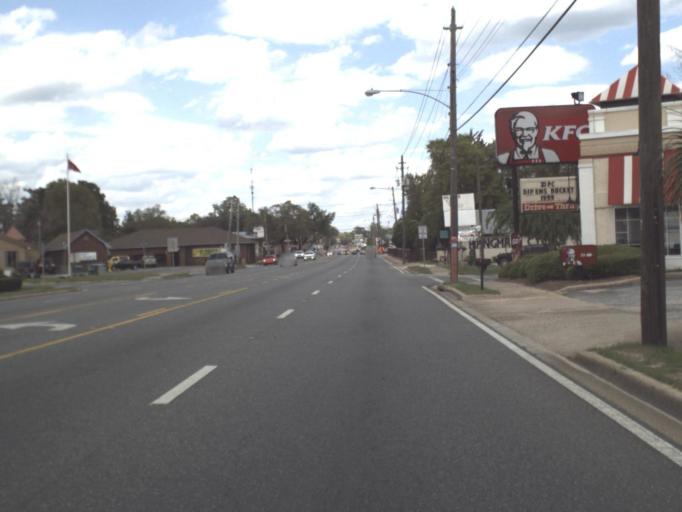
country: US
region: Florida
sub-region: Okaloosa County
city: Crestview
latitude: 30.7649
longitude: -86.5690
